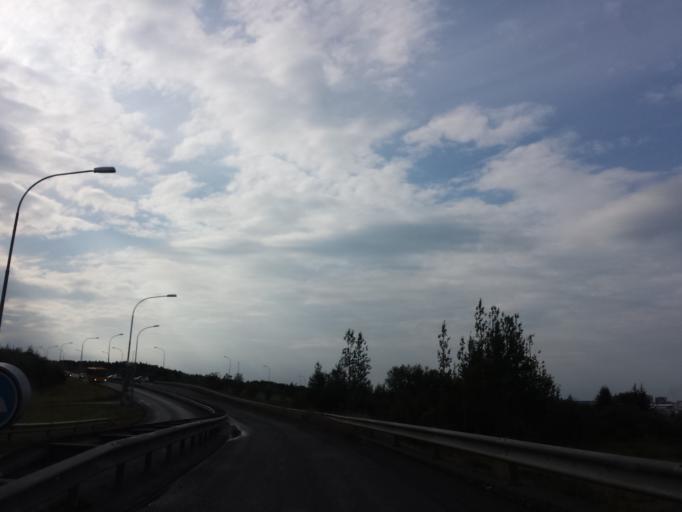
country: IS
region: Capital Region
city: Reykjavik
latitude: 64.1152
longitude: -21.8210
